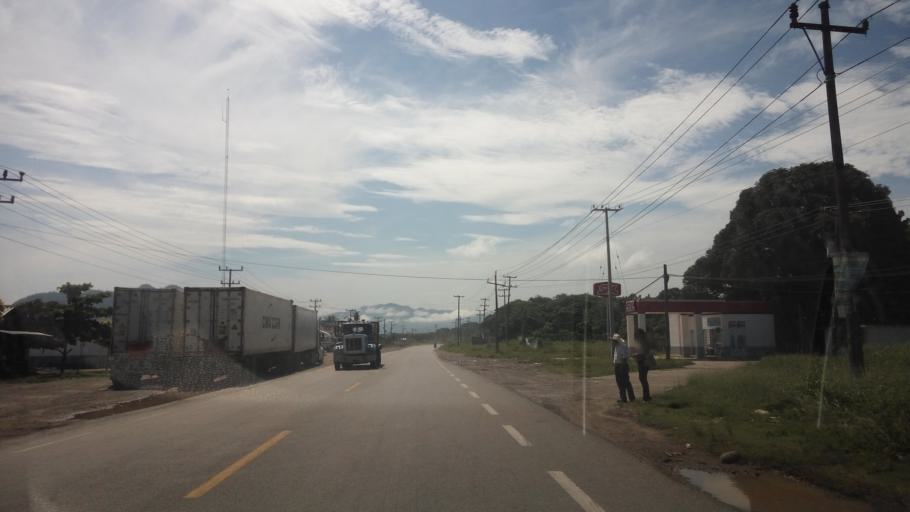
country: MX
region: Tabasco
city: Teapa
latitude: 17.5799
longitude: -92.9631
